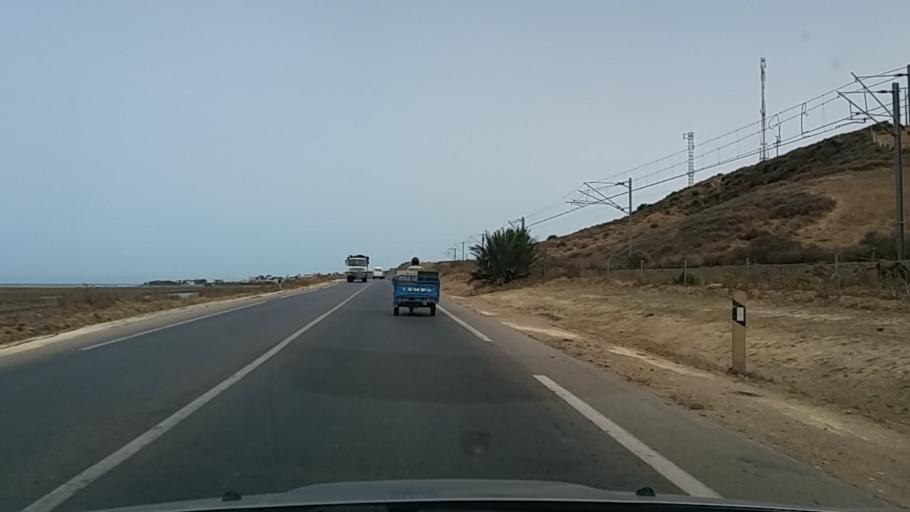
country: MA
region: Tanger-Tetouan
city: Asilah
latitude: 35.5148
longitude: -5.9980
